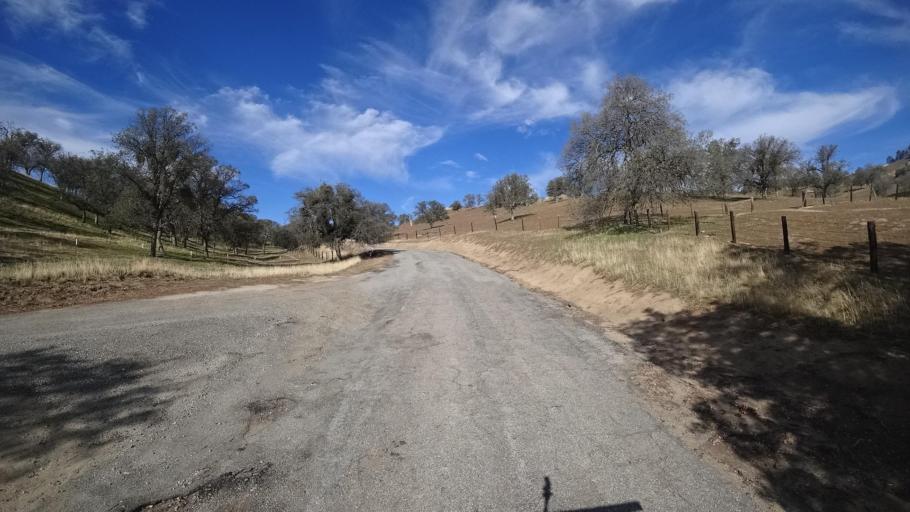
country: US
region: California
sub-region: Kern County
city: Oildale
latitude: 35.5641
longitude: -118.7946
